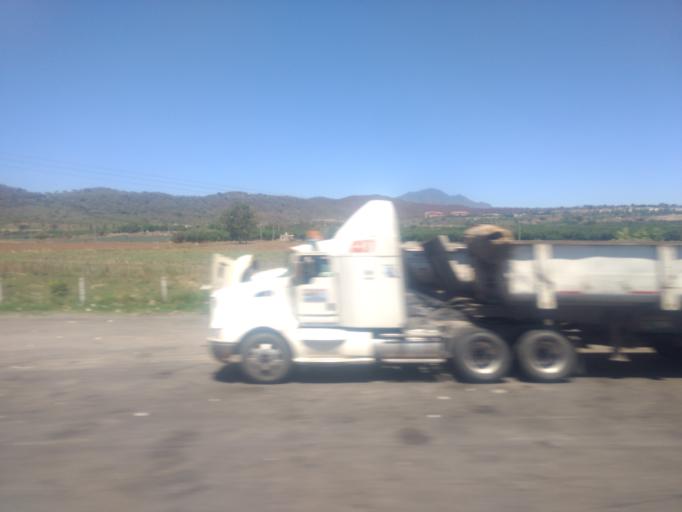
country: MX
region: Jalisco
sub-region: Acatlan de Juarez
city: Villa de los Ninos
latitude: 20.4137
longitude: -103.5577
